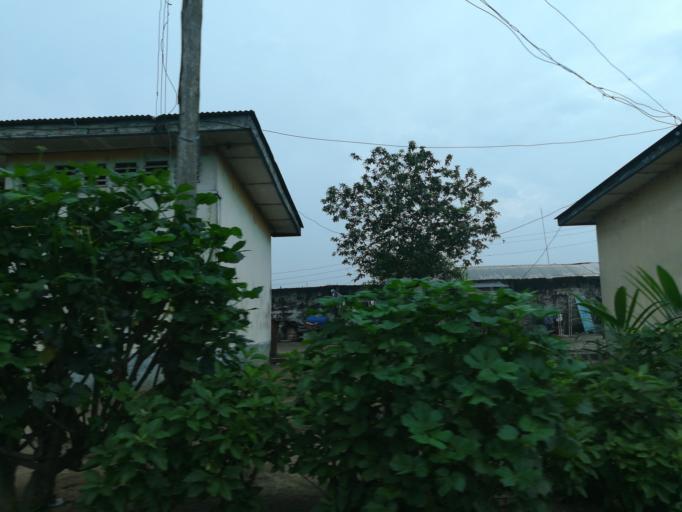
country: NG
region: Rivers
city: Port Harcourt
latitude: 4.7575
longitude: 7.0149
